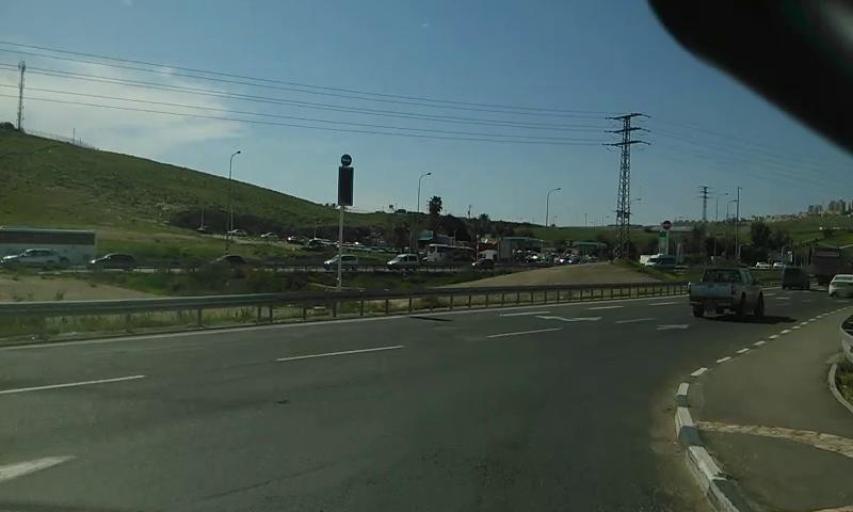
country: PS
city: Az Za`ayyim
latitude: 31.8058
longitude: 35.3259
